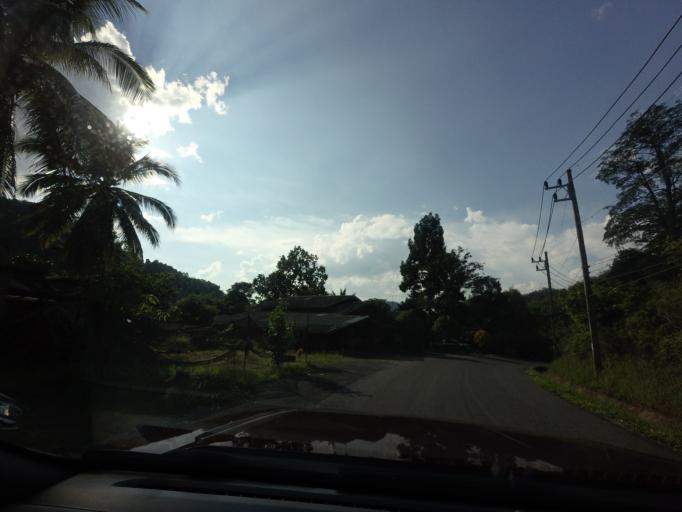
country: TH
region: Yala
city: Than To
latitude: 6.1518
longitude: 101.2809
